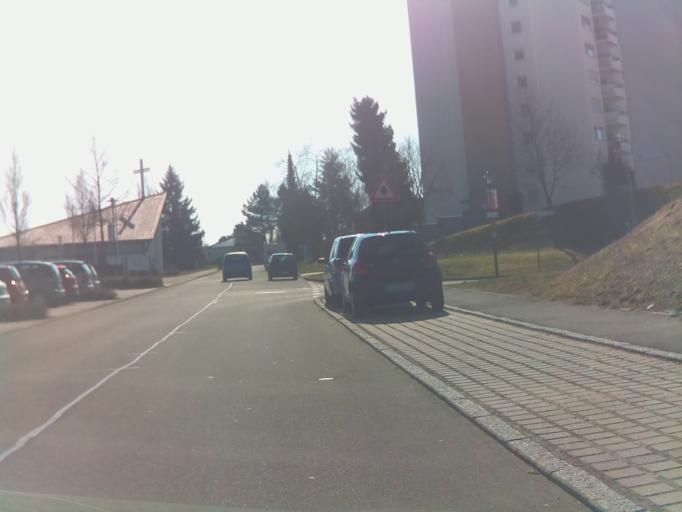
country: DE
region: Baden-Wuerttemberg
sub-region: Karlsruhe Region
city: Horb am Neckar
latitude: 48.4519
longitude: 8.6880
